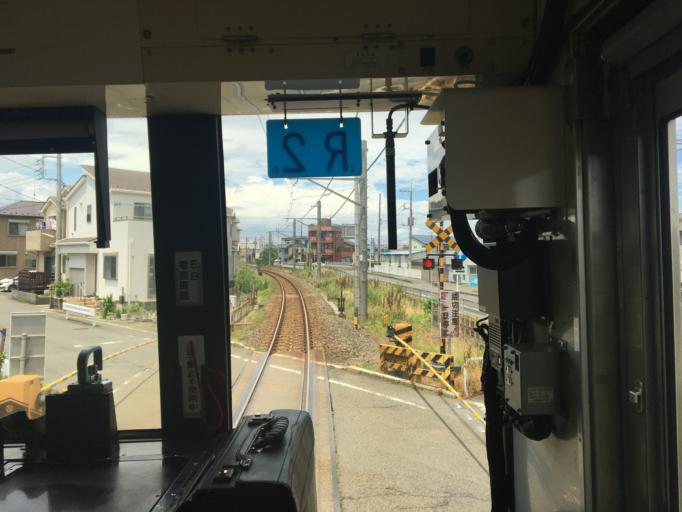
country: JP
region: Kanagawa
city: Atsugi
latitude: 35.4040
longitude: 139.3816
